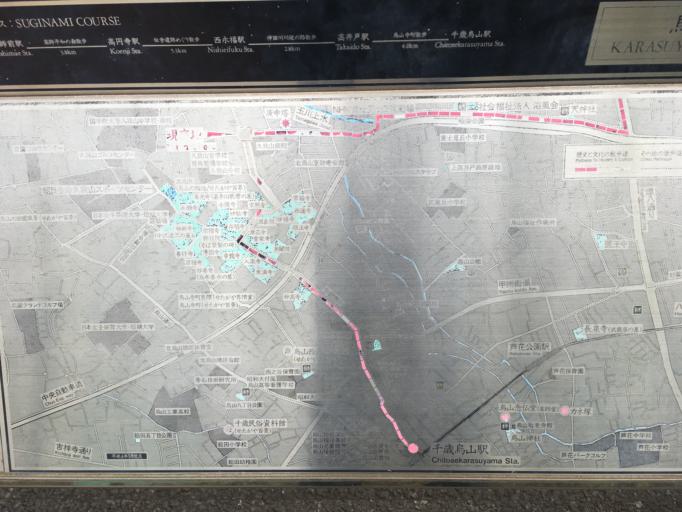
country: JP
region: Tokyo
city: Mitaka-shi
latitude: 35.6819
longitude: 139.5984
